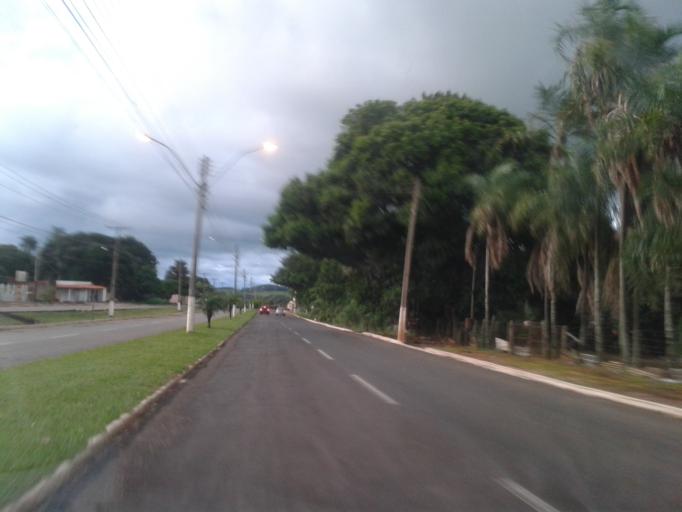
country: BR
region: Goias
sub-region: Morrinhos
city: Morrinhos
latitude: -17.7310
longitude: -49.1475
